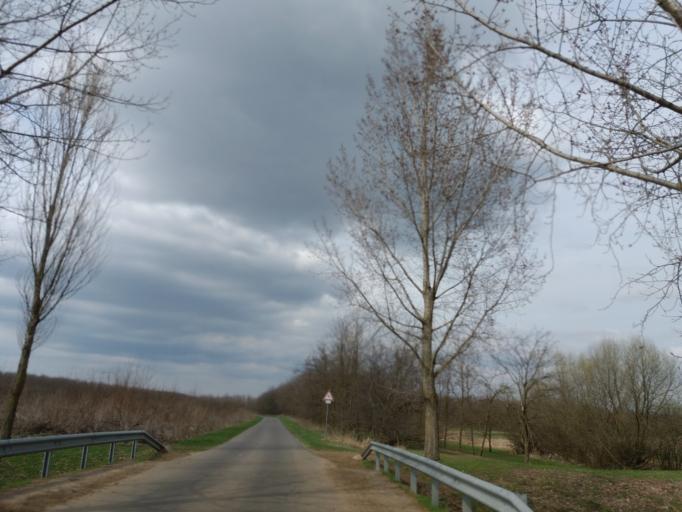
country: HU
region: Szabolcs-Szatmar-Bereg
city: Petnehaza
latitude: 48.0671
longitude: 22.0462
